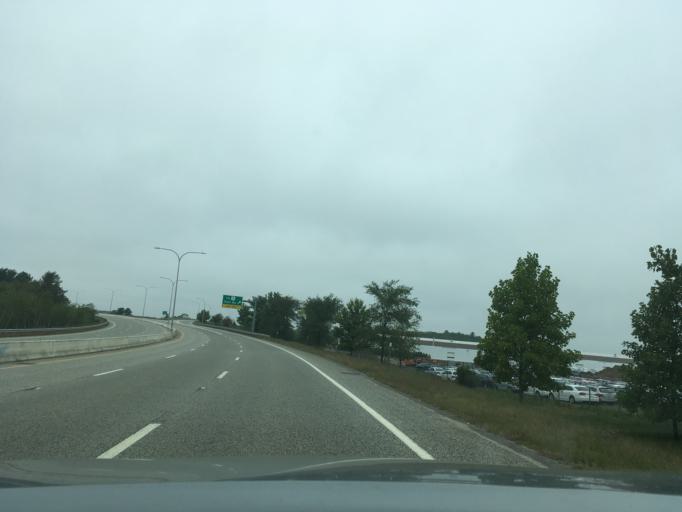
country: US
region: Rhode Island
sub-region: Washington County
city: North Kingstown
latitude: 41.6016
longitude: -71.4448
